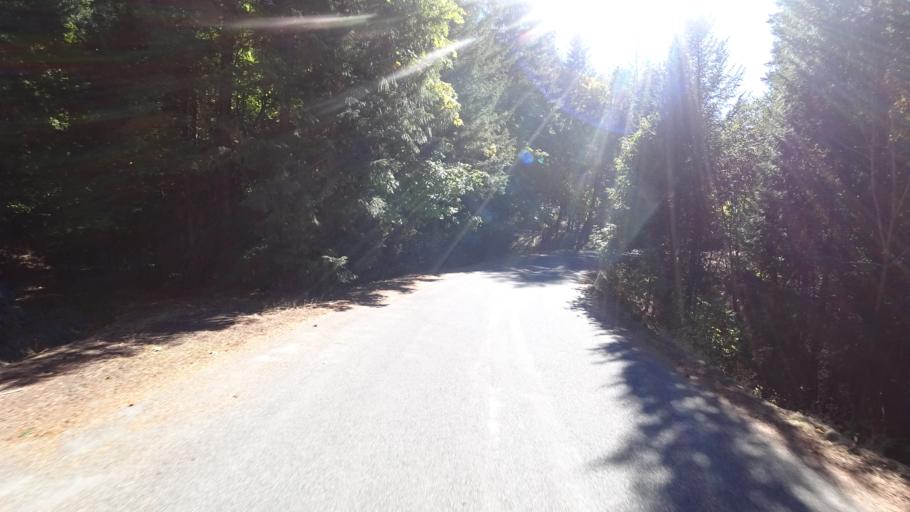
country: US
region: California
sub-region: Siskiyou County
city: Yreka
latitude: 41.3592
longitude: -123.0315
